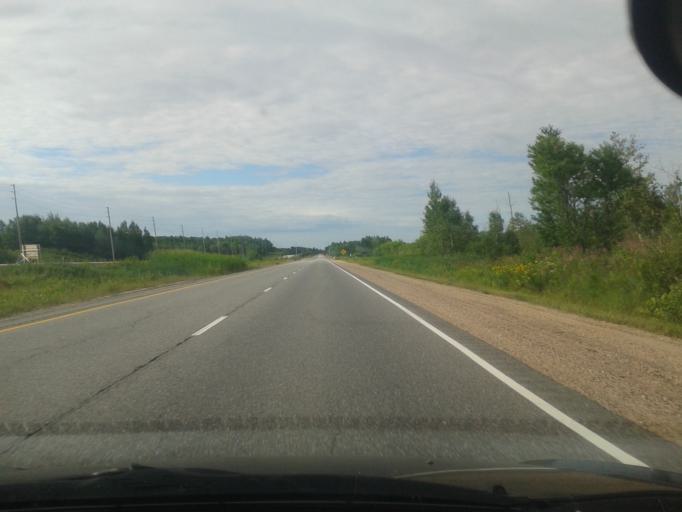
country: CA
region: Ontario
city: Powassan
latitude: 46.1489
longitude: -79.3599
